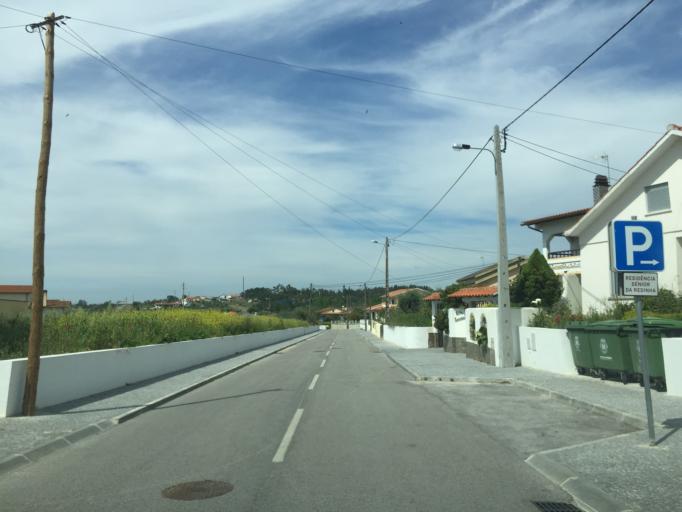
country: PT
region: Coimbra
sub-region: Soure
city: Soure
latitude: 40.0073
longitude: -8.5804
